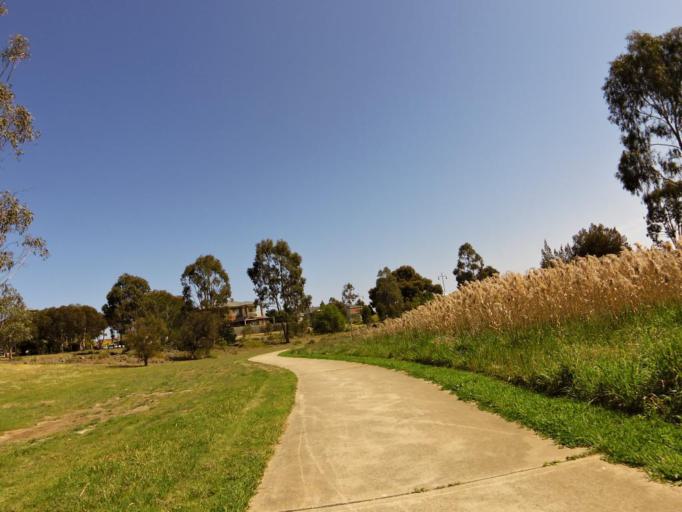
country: AU
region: Victoria
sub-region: Wyndham
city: Williams Landing
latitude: -37.8766
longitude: 144.7388
